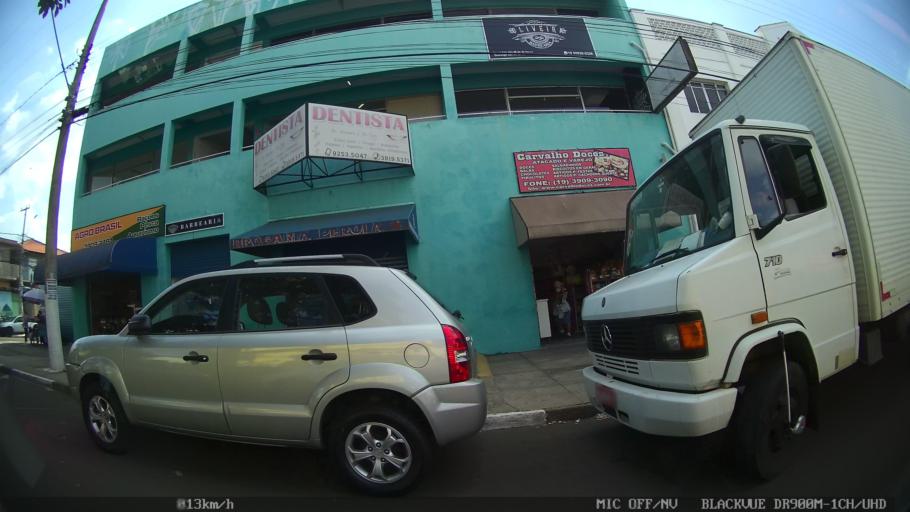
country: BR
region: Sao Paulo
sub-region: Hortolandia
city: Hortolandia
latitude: -22.9013
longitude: -47.2390
